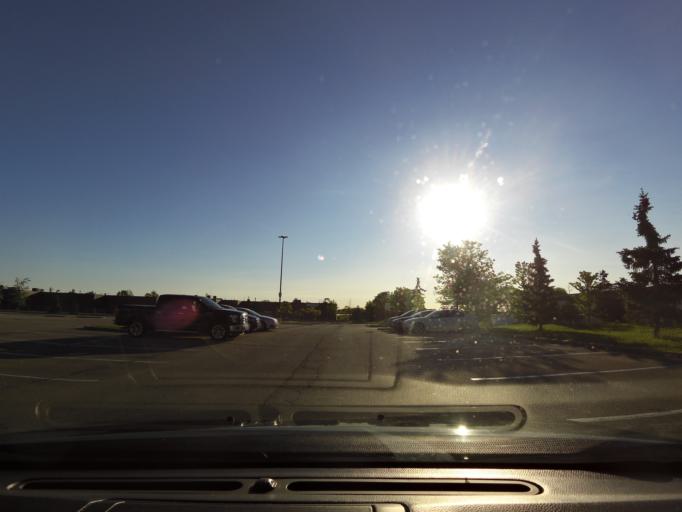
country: CA
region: Ontario
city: Mississauga
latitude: 43.6016
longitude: -79.7370
